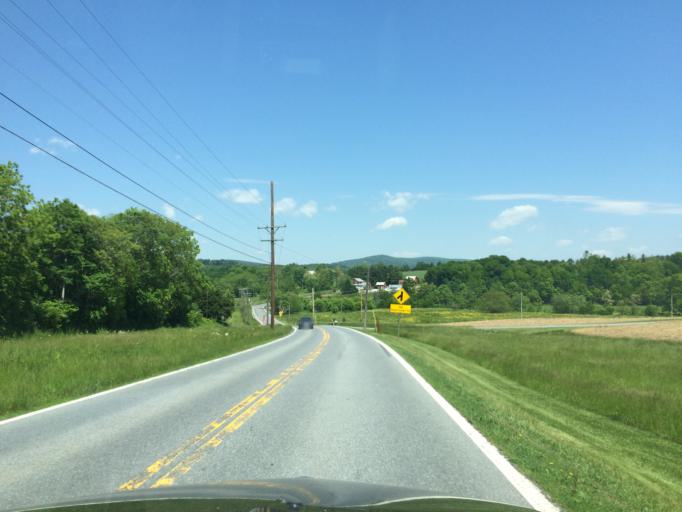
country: US
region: Maryland
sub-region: Frederick County
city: Myersville
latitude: 39.4848
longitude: -77.5643
